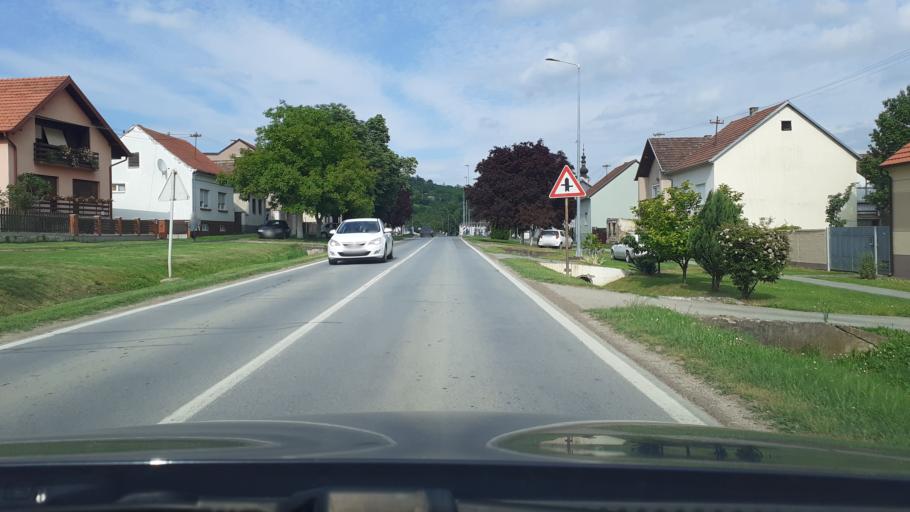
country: HR
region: Brodsko-Posavska
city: Sibinj
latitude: 45.1899
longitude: 17.9061
